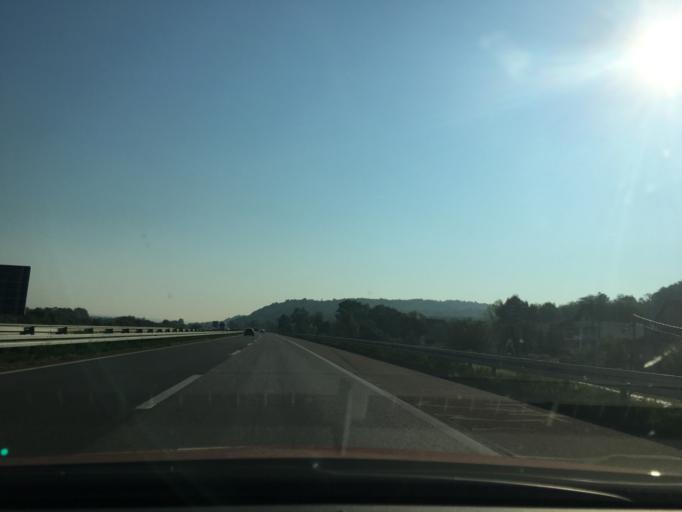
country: RS
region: Central Serbia
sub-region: Belgrade
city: Grocka
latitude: 44.5752
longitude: 20.7538
